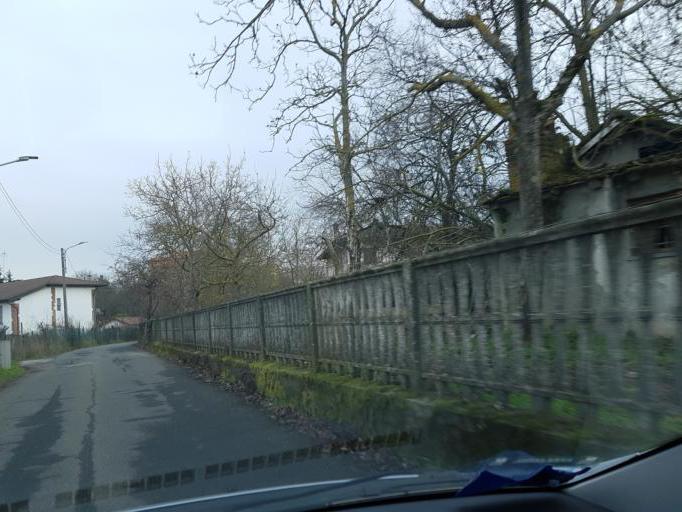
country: IT
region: Piedmont
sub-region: Provincia di Alessandria
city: Novi Ligure
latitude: 44.7697
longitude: 8.7982
